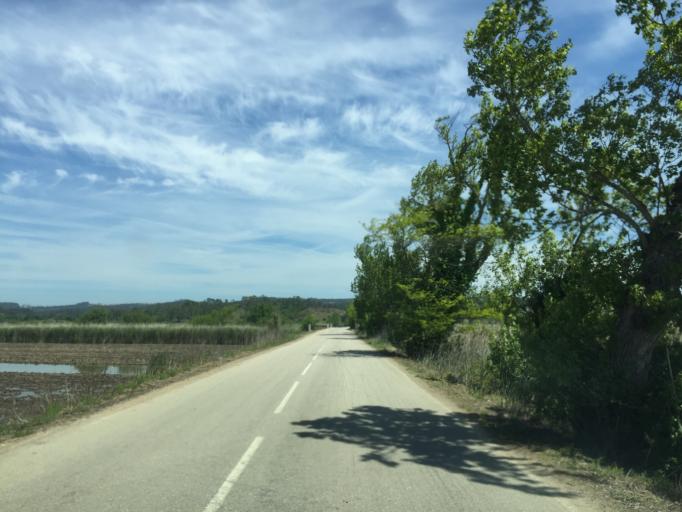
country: PT
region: Leiria
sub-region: Pombal
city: Lourical
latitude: 40.0695
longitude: -8.7431
